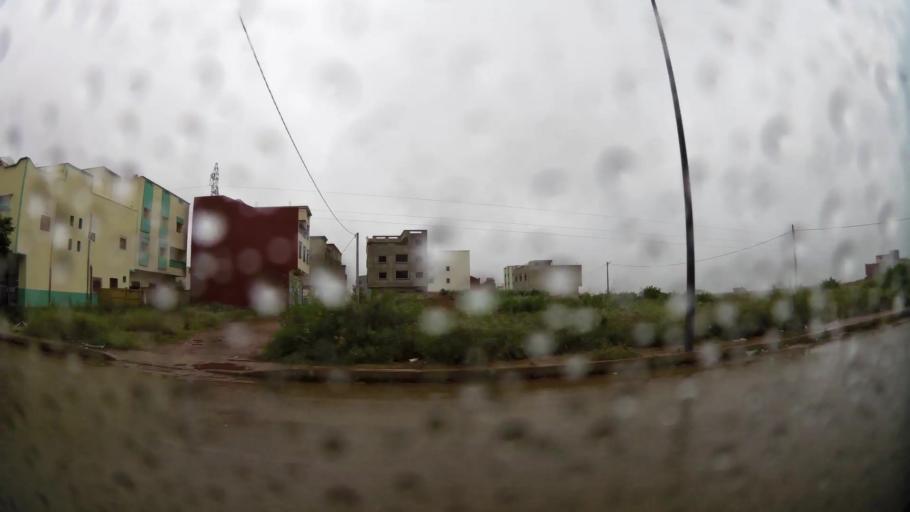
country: MA
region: Oriental
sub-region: Nador
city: Boudinar
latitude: 35.1160
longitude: -3.6439
